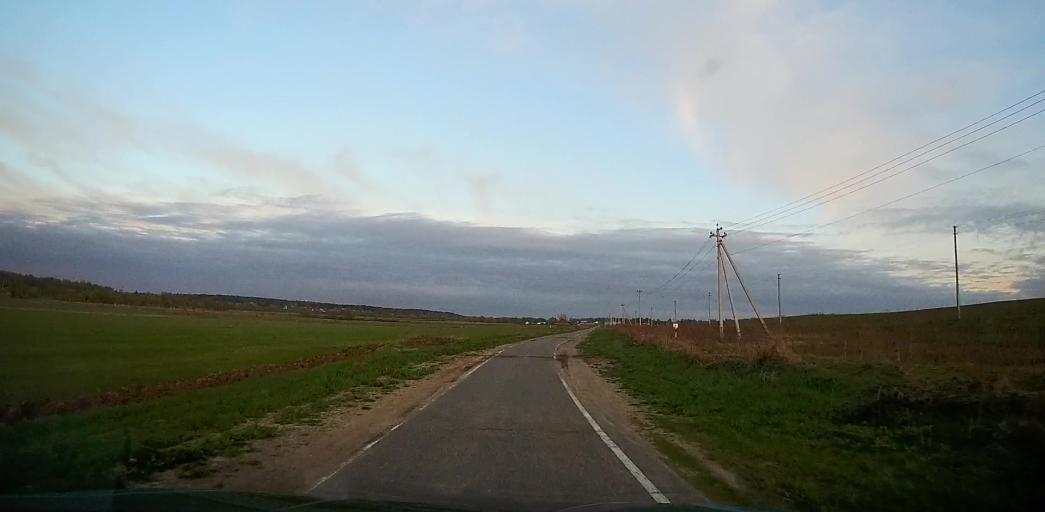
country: RU
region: Moskovskaya
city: Peski
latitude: 55.2249
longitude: 38.7355
